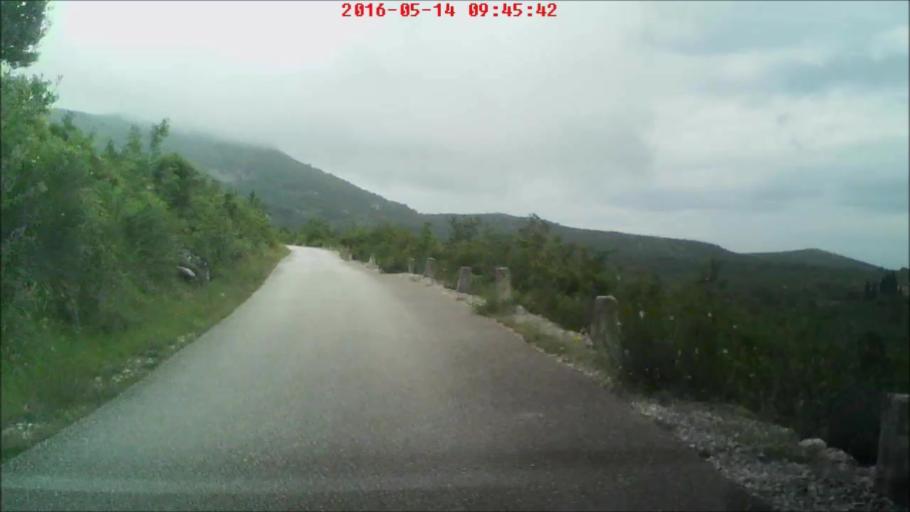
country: HR
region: Dubrovacko-Neretvanska
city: Podgora
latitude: 42.7812
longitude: 17.9121
